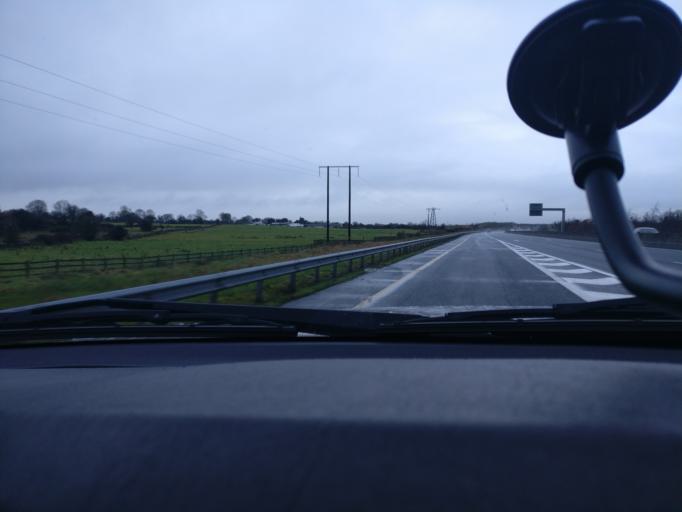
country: IE
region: Connaught
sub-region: County Galway
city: Loughrea
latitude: 53.2647
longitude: -8.6158
